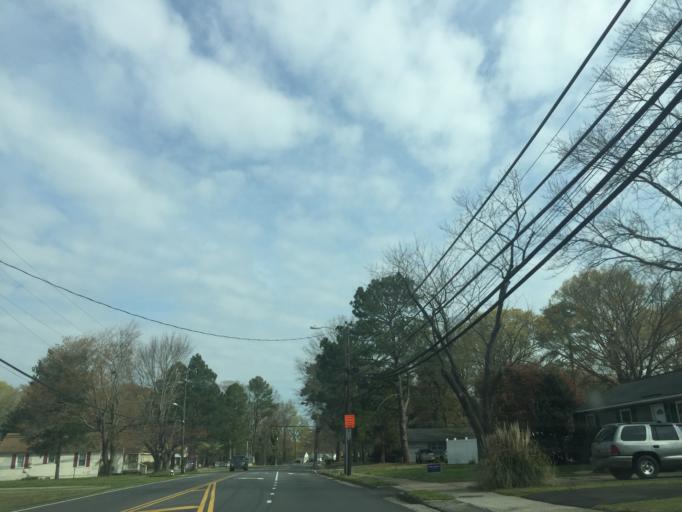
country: US
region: Virginia
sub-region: City of Newport News
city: Newport News
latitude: 37.0729
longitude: -76.4577
